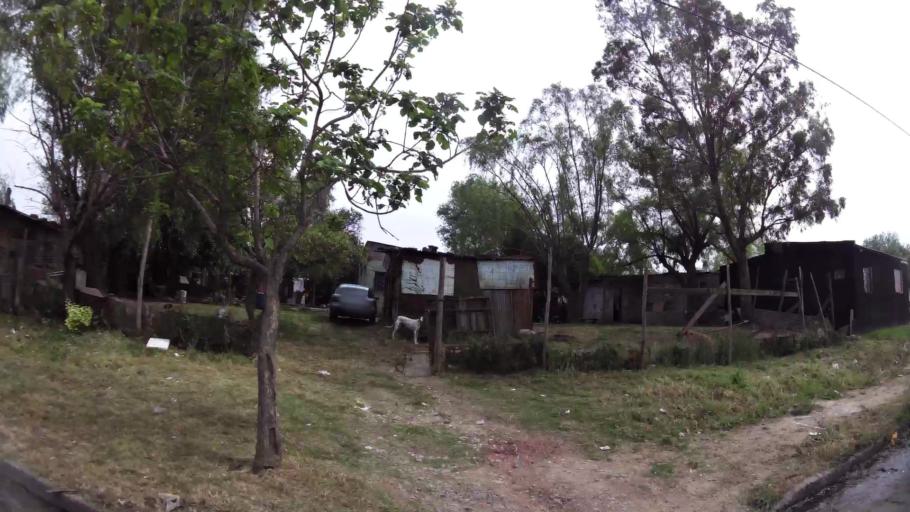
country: UY
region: Montevideo
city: Montevideo
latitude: -34.8364
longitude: -56.1771
